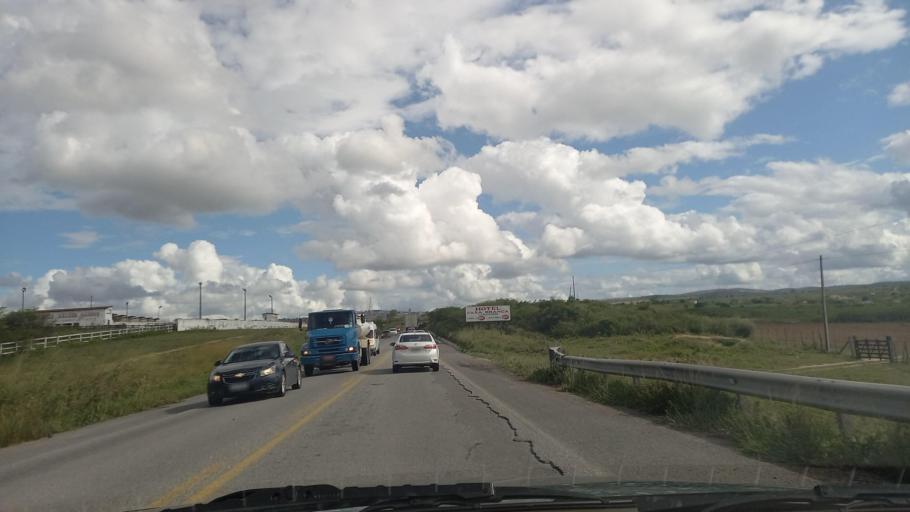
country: BR
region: Pernambuco
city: Garanhuns
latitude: -8.8222
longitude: -36.4490
